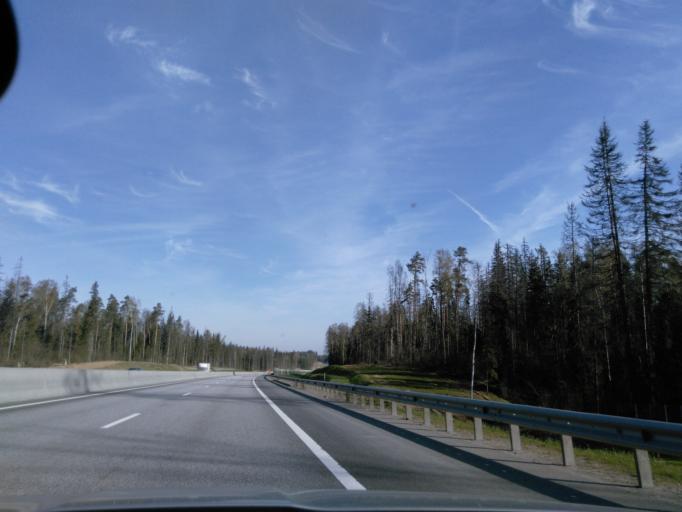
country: RU
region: Moskovskaya
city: Rzhavki
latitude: 56.0261
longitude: 37.2732
